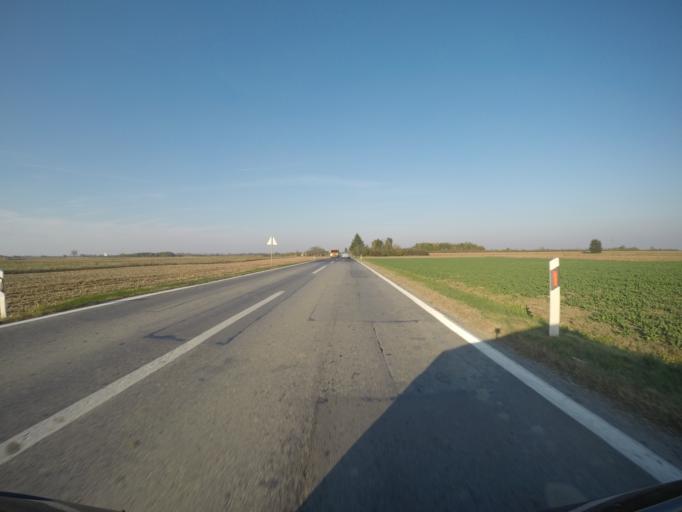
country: HU
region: Somogy
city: Barcs
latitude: 45.9212
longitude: 17.4521
